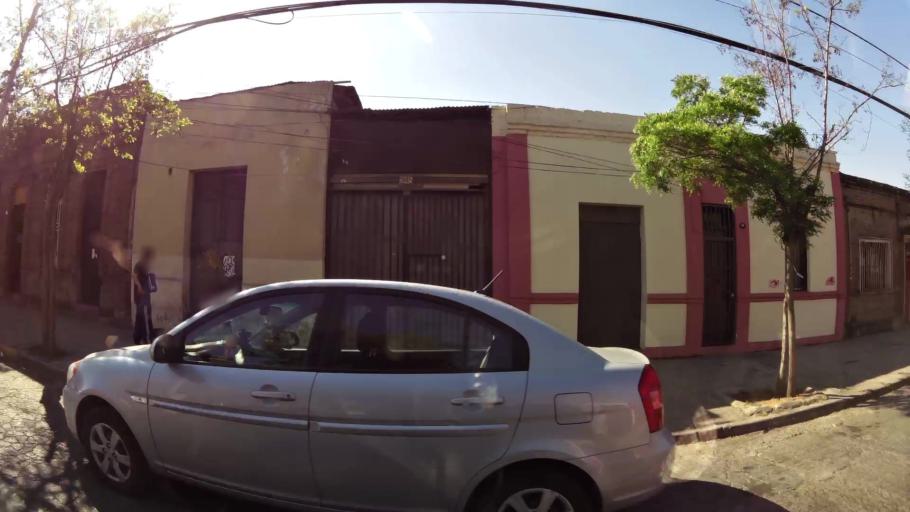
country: CL
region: Santiago Metropolitan
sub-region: Provincia de Santiago
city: Santiago
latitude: -33.4079
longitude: -70.6362
